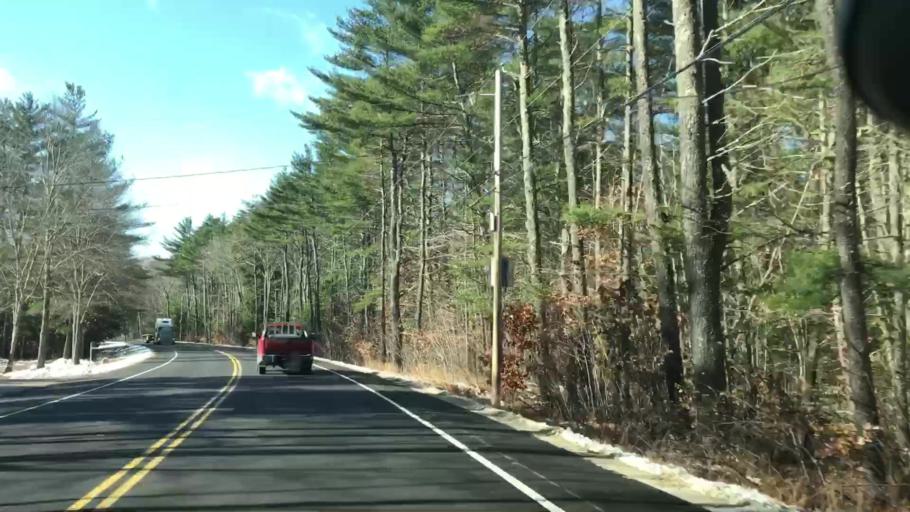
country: US
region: New Hampshire
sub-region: Carroll County
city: Freedom
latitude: 43.7982
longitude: -71.0065
